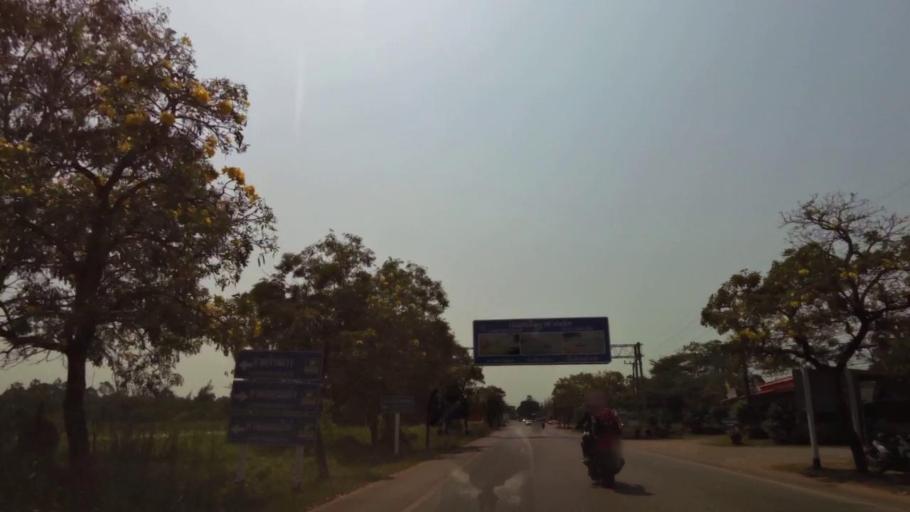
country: TH
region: Chanthaburi
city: Tha Mai
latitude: 12.5649
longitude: 101.9141
